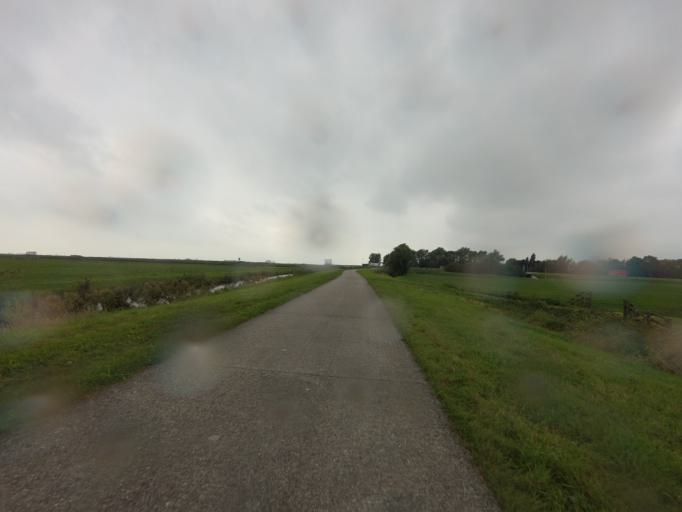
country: NL
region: Friesland
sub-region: Sudwest Fryslan
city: Koudum
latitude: 52.9464
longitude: 5.4392
